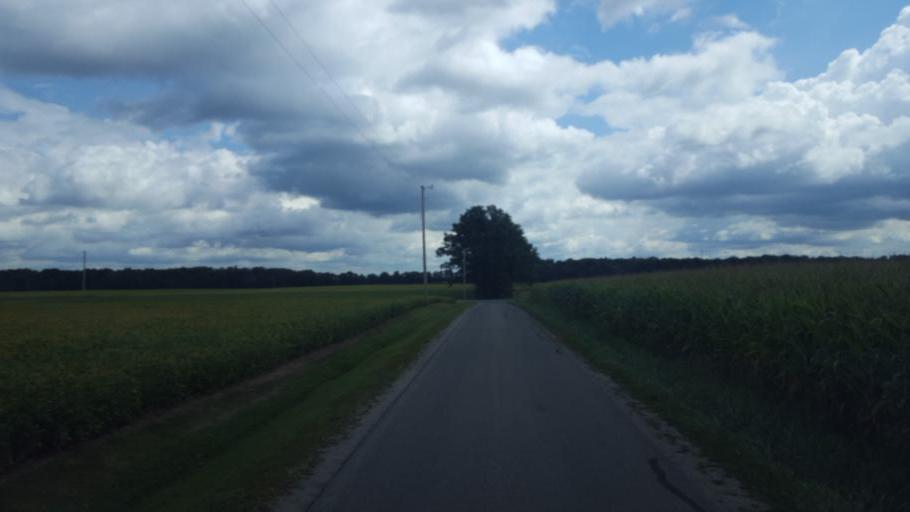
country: US
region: Ohio
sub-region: Huron County
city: Willard
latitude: 41.1150
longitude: -82.7566
